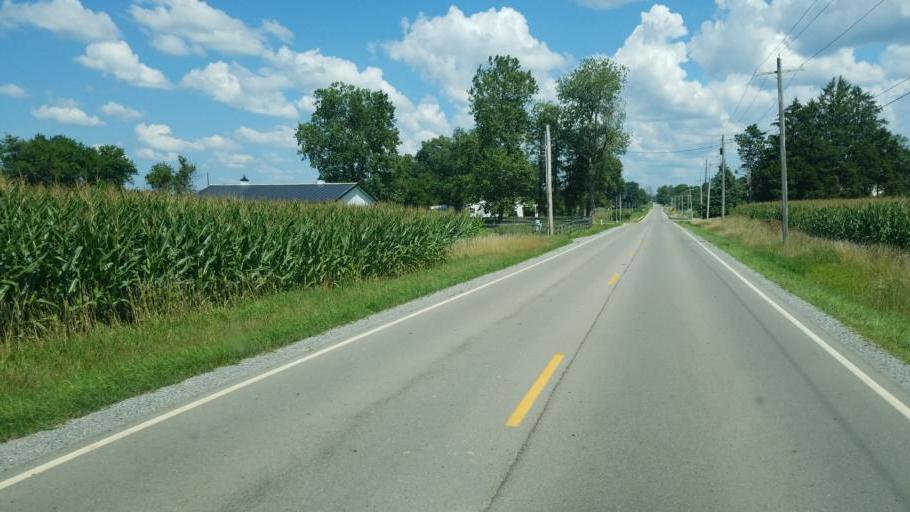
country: US
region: Ohio
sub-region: Crawford County
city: Galion
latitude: 40.7333
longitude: -82.7489
